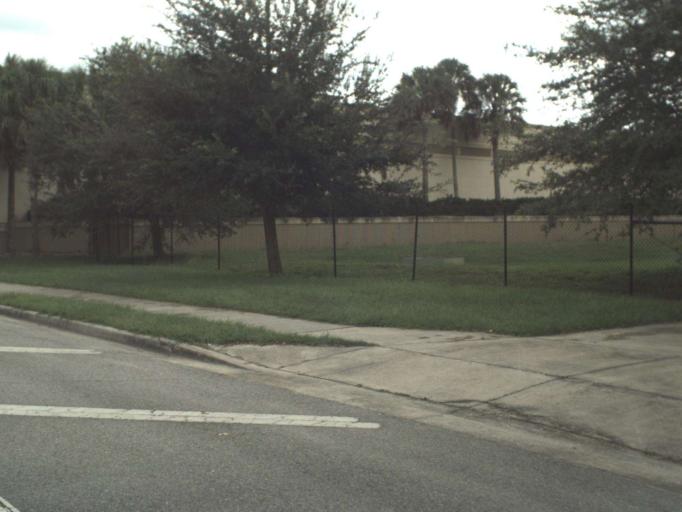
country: US
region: Florida
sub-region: Orange County
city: Orlando
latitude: 28.5379
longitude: -81.3643
